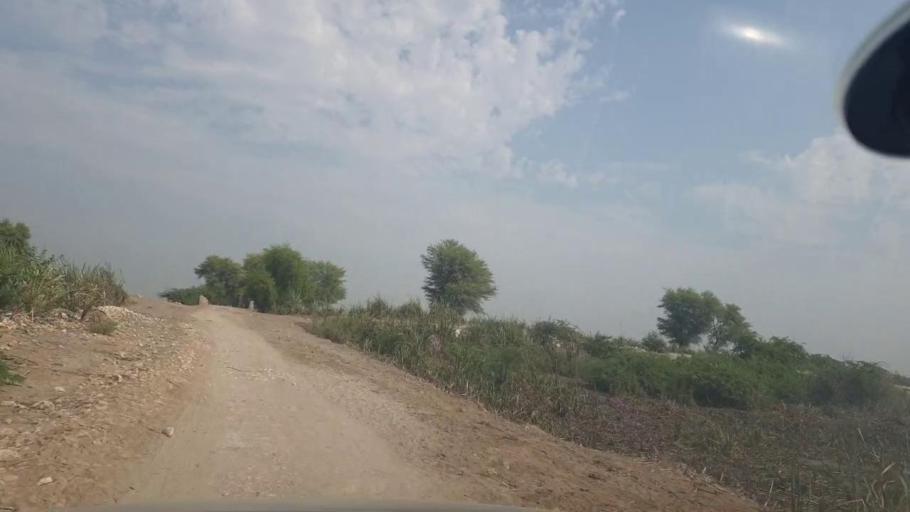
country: PK
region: Balochistan
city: Mehrabpur
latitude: 28.1169
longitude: 68.0914
